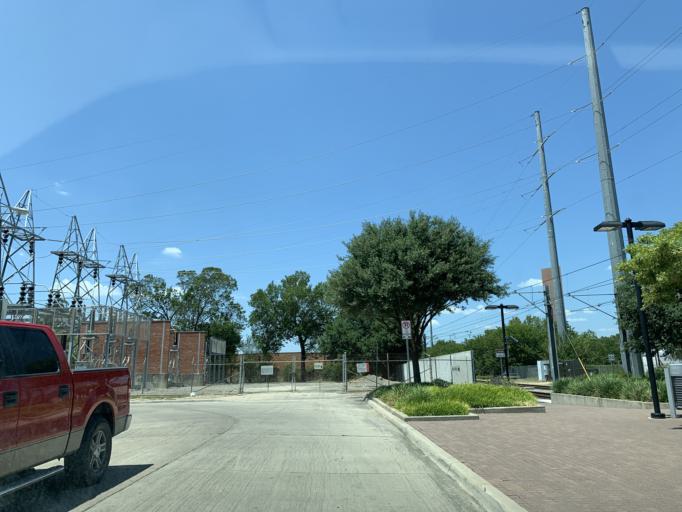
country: US
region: Texas
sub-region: Dallas County
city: Dallas
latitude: 32.7739
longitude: -96.7650
